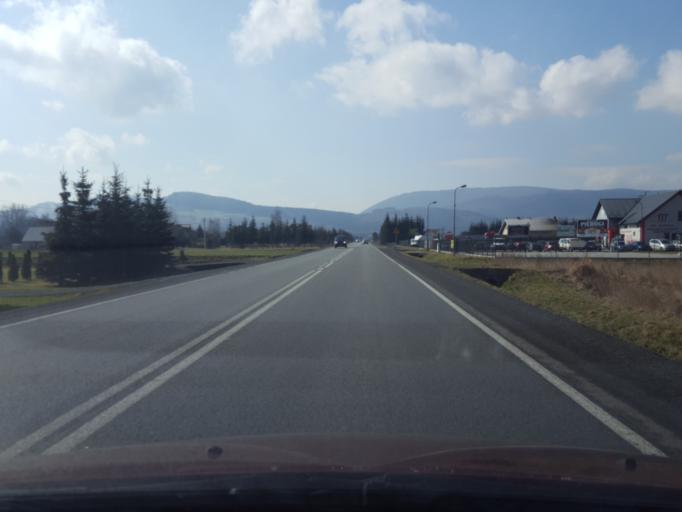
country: PL
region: Lesser Poland Voivodeship
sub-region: Powiat nowosadecki
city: Lososina Dolna
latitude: 49.7549
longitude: 20.6355
